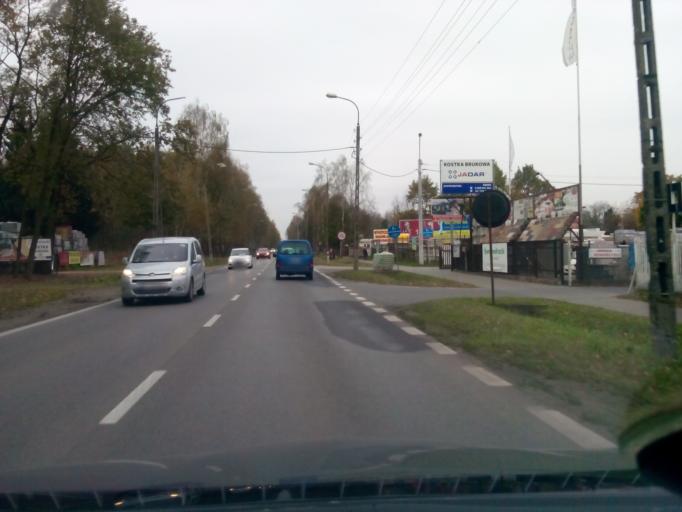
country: PL
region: Masovian Voivodeship
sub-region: Powiat grodziski
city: Milanowek
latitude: 52.1120
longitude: 20.6591
